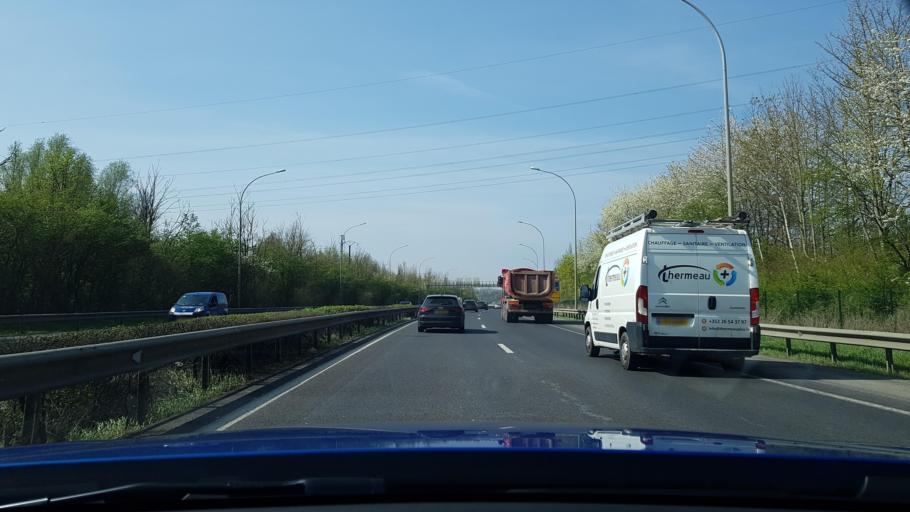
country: LU
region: Luxembourg
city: Pontpierre
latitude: 49.5280
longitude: 6.0141
